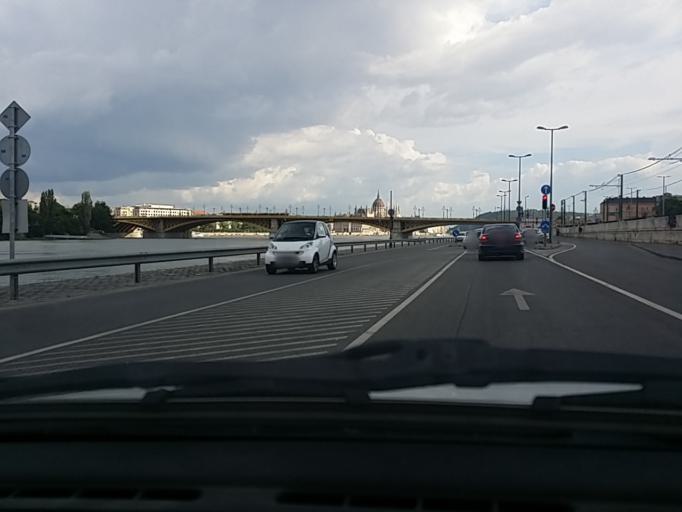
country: HU
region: Budapest
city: Budapest II. keruelet
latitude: 47.5182
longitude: 19.0392
